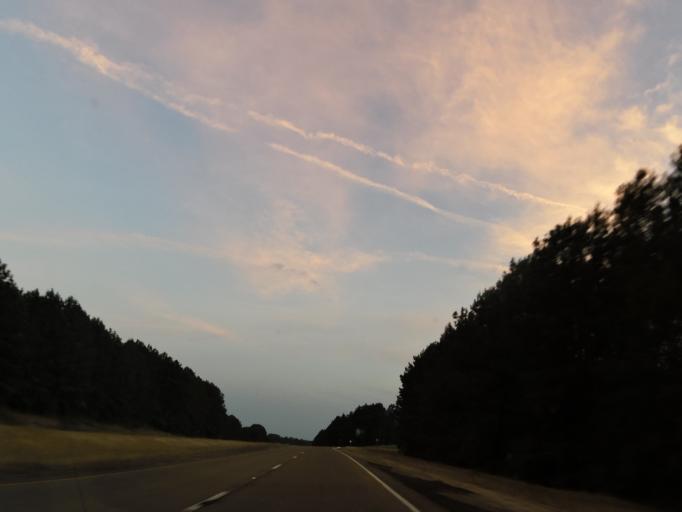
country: US
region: Mississippi
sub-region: Lauderdale County
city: Meridian Station
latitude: 32.6125
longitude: -88.4992
